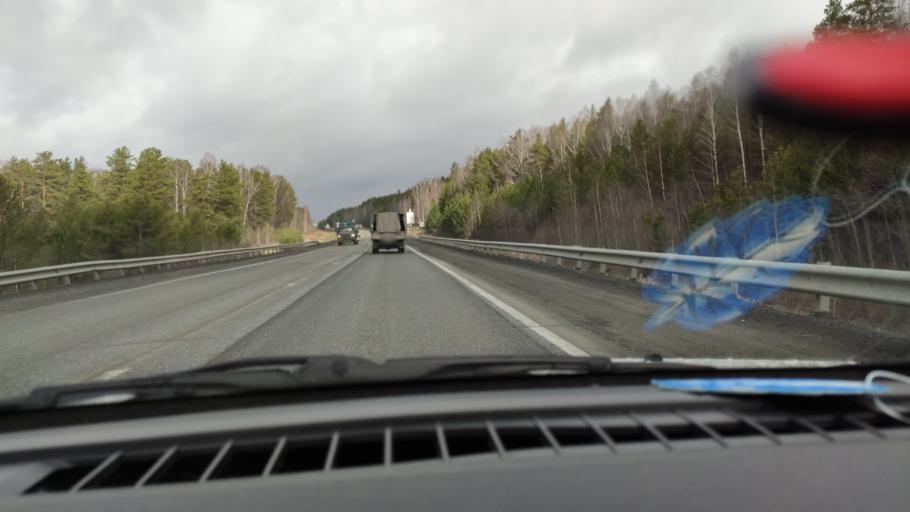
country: RU
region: Sverdlovsk
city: Talitsa
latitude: 56.8686
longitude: 60.0432
